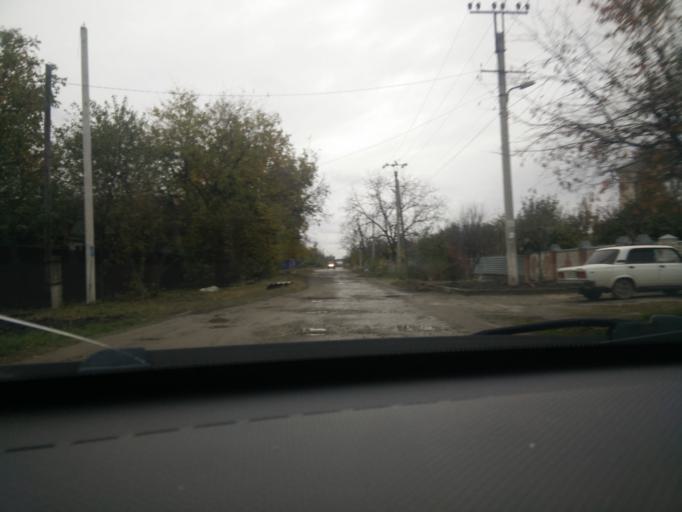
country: RU
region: Stavropol'skiy
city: Ivanovskoye
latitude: 44.5752
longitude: 41.8787
